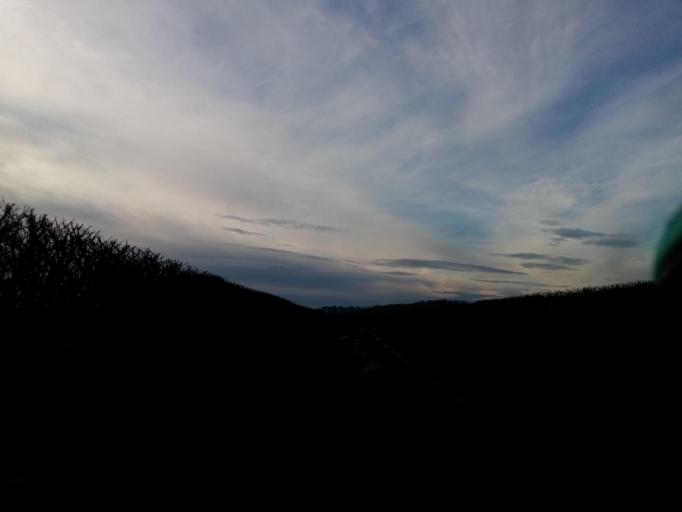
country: GB
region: Scotland
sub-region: The Scottish Borders
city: Hawick
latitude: 55.4524
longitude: -2.7335
